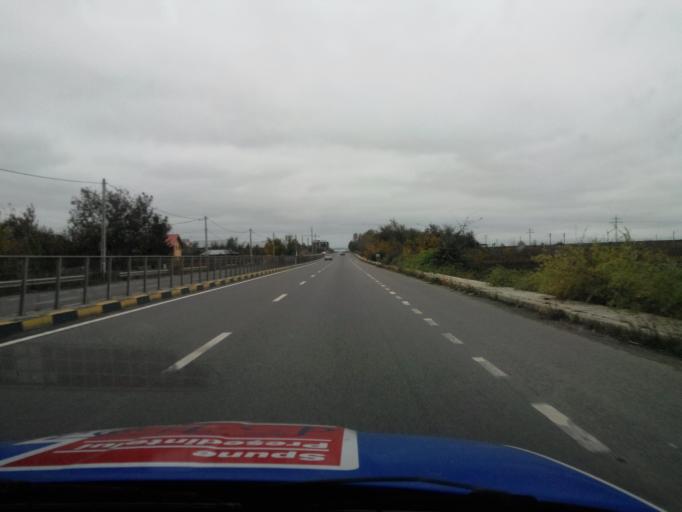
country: RO
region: Giurgiu
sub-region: Comuna Calugareni
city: Calugareni
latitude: 44.1930
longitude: 26.0073
